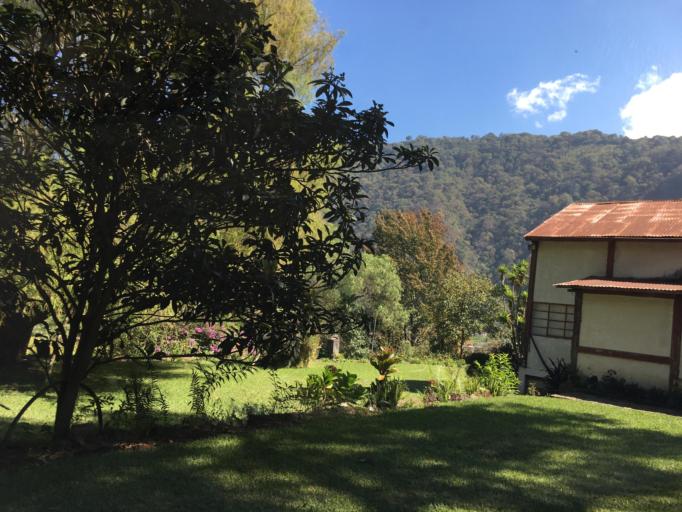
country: GT
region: Solola
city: San Lucas Toliman
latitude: 14.6367
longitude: -91.1397
